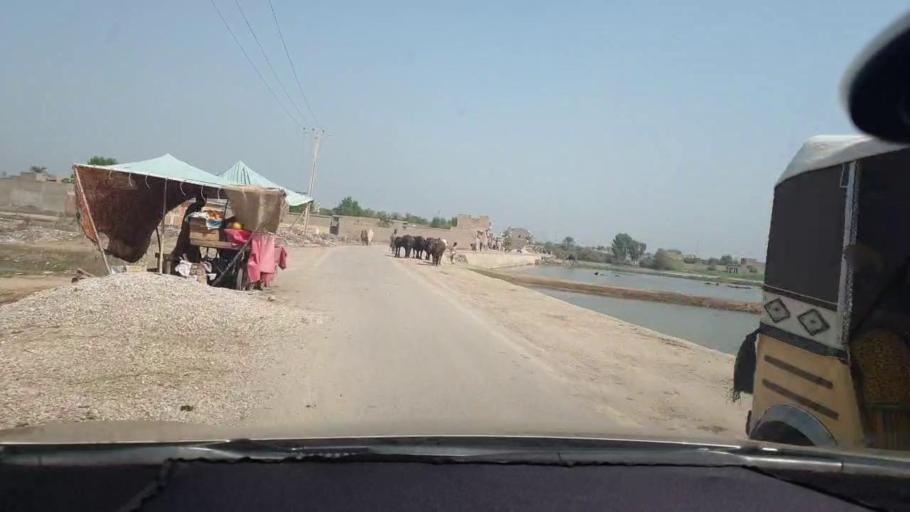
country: PK
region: Sindh
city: Kambar
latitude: 27.5773
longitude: 68.0071
